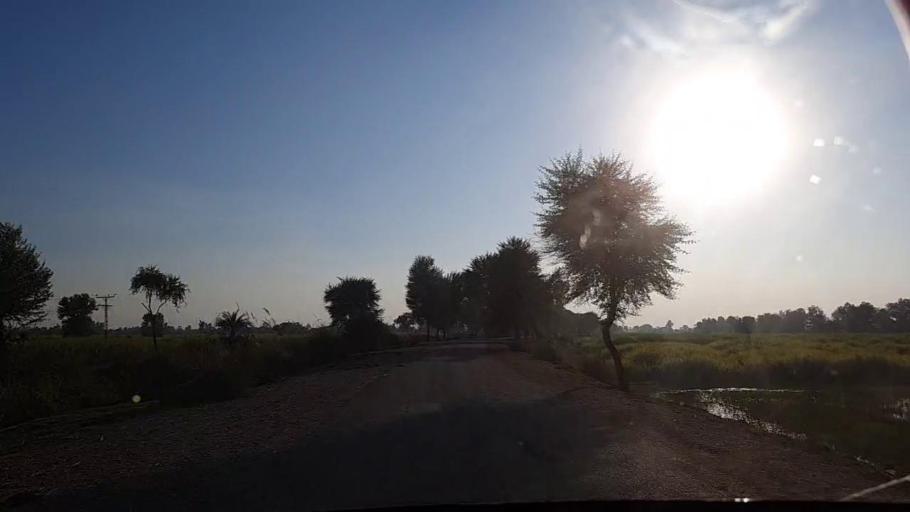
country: PK
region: Sindh
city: Sobhadero
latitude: 27.4188
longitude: 68.4039
